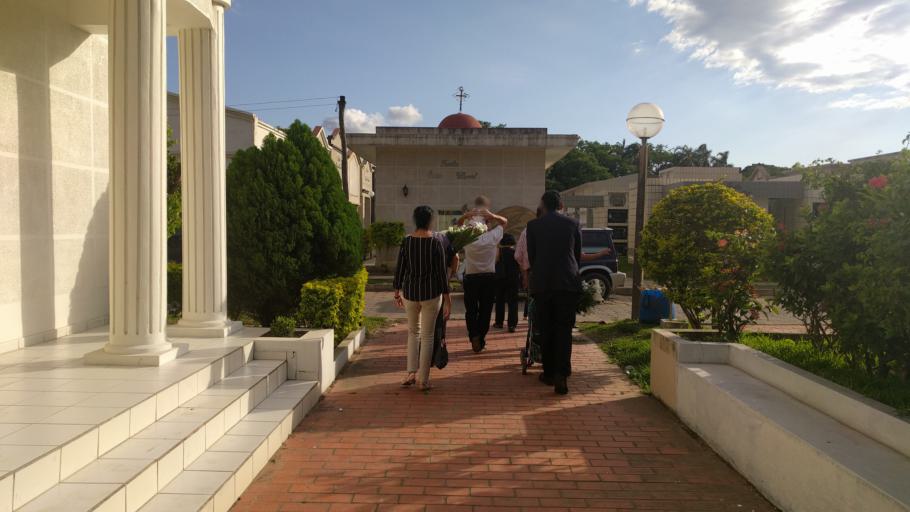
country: BO
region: Santa Cruz
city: Santa Cruz de la Sierra
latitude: -17.7482
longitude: -63.1612
